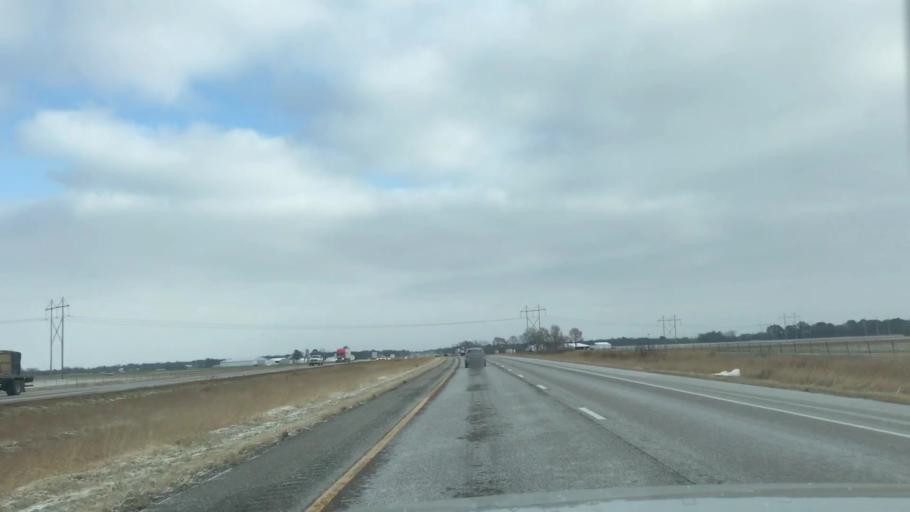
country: US
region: Illinois
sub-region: Madison County
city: Worden
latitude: 38.9410
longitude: -89.7886
